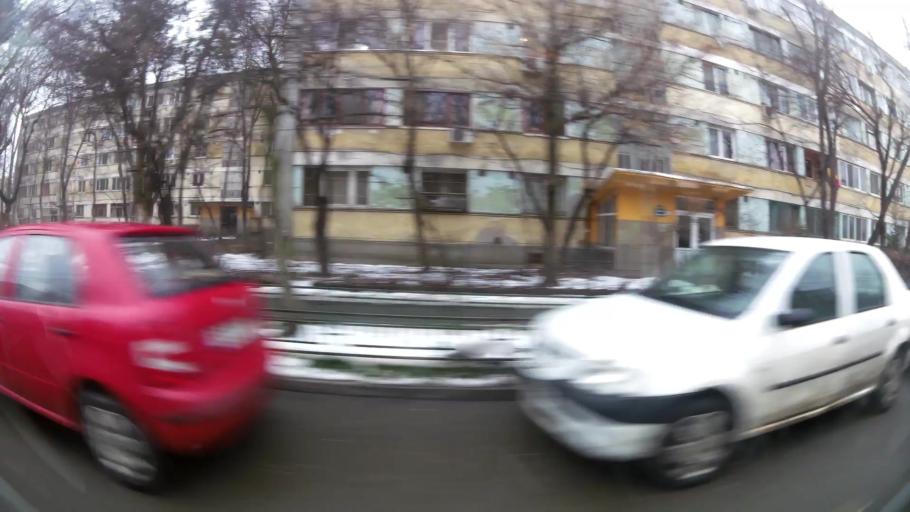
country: RO
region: Ilfov
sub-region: Comuna Chiajna
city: Rosu
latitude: 44.4608
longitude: 26.0404
